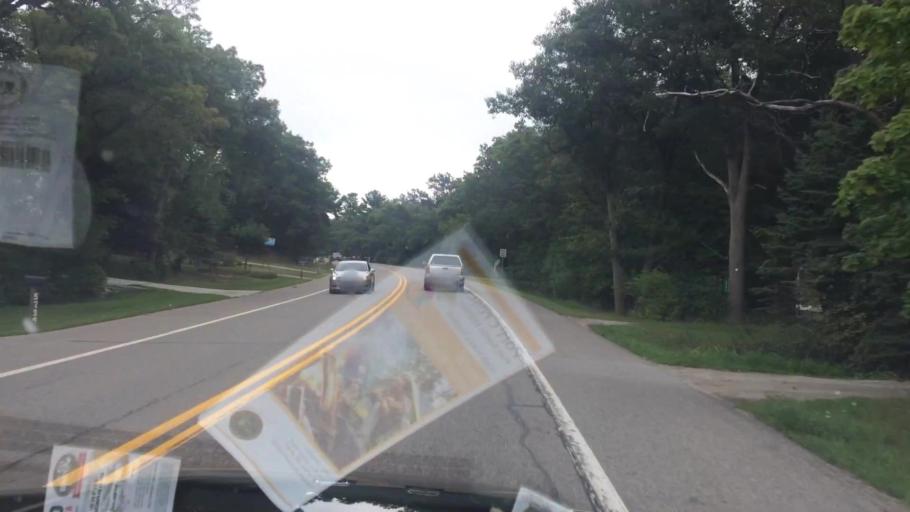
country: US
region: Michigan
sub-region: Huron County
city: Pigeon
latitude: 43.9747
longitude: -83.2479
